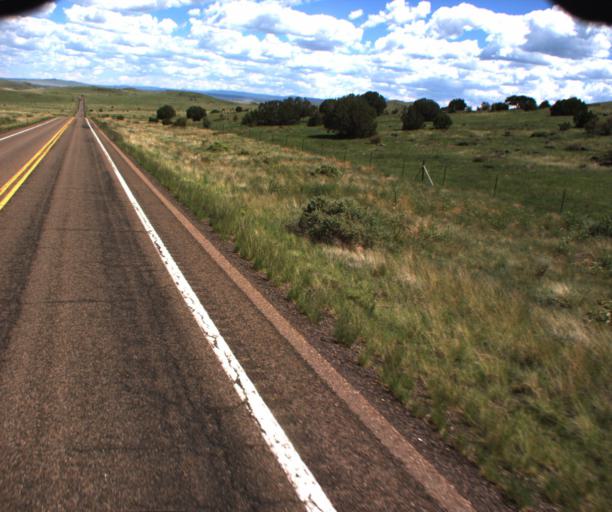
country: US
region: Arizona
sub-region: Apache County
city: Springerville
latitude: 34.2179
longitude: -109.4703
